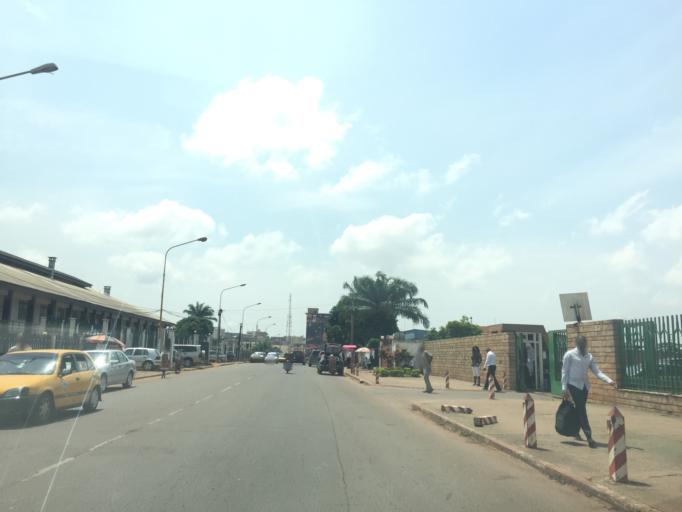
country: CM
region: Centre
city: Yaounde
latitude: 3.8683
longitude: 11.5231
